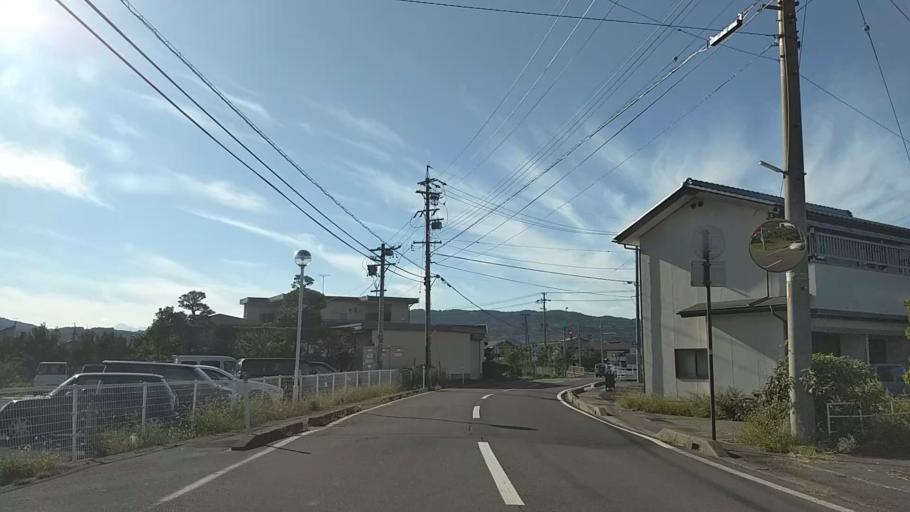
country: JP
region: Nagano
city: Nagano-shi
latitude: 36.5651
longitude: 138.1477
